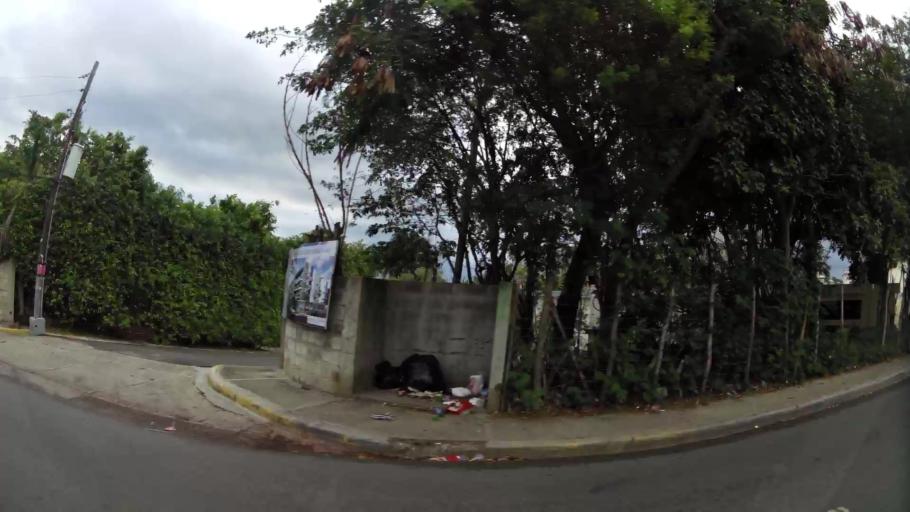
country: DO
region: Nacional
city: Santo Domingo
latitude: 18.5106
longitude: -69.9616
